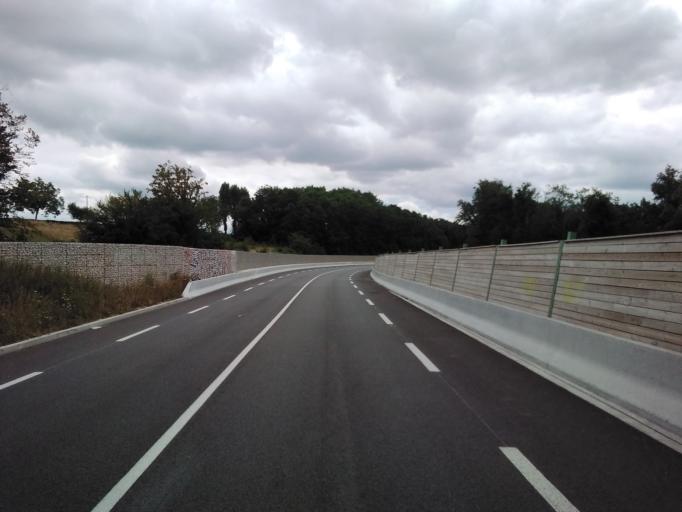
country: FR
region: Rhone-Alpes
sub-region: Departement de l'Ain
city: Montagnat
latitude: 46.1934
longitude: 5.2702
